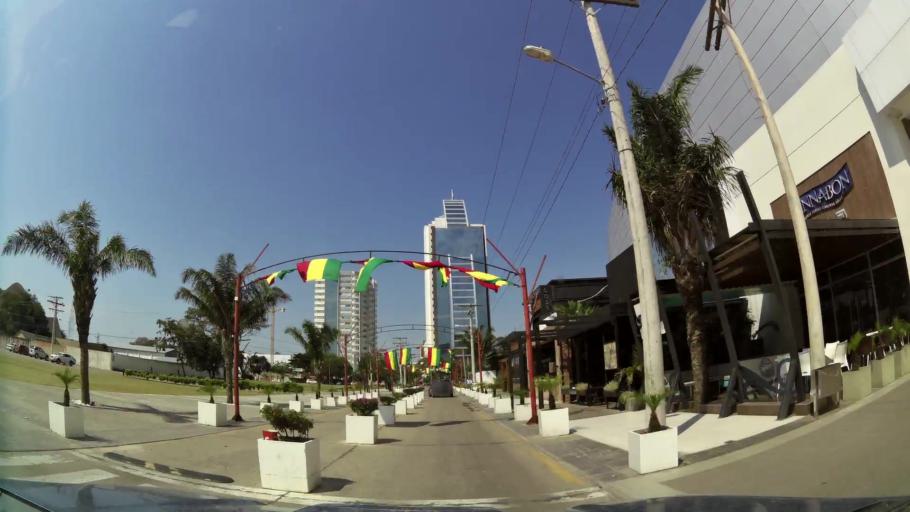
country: BO
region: Santa Cruz
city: Santa Cruz de la Sierra
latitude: -17.7536
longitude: -63.1991
